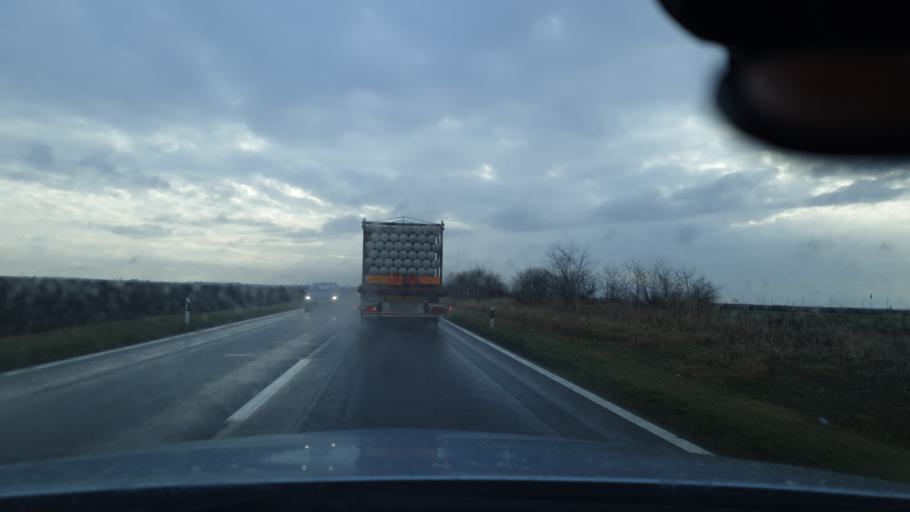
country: RS
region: Autonomna Pokrajina Vojvodina
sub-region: Juznobanatski Okrug
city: Kovin
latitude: 44.7871
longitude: 20.9217
